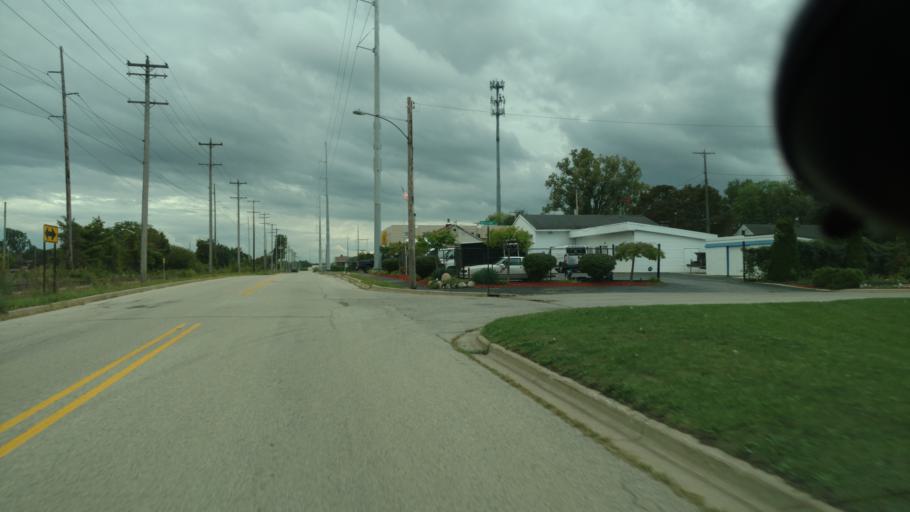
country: US
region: Michigan
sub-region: Ingham County
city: Edgemont Park
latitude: 42.7322
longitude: -84.5822
